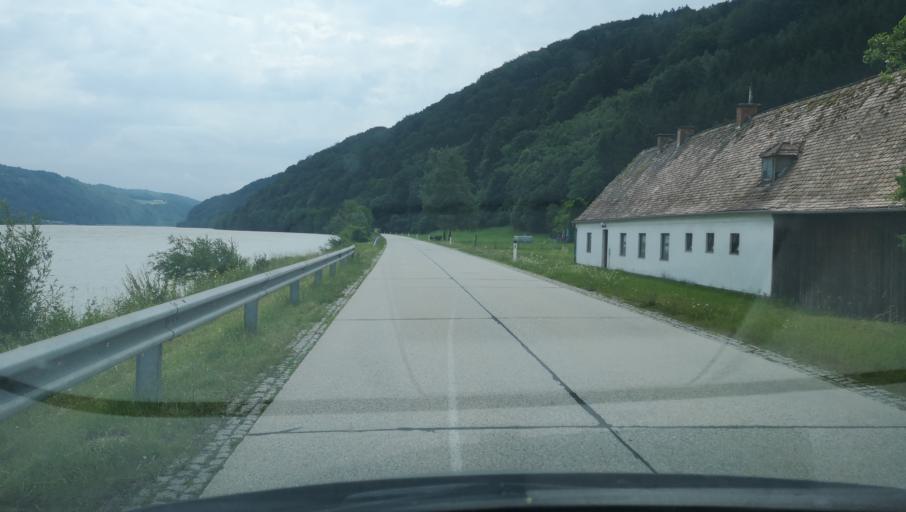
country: AT
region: Lower Austria
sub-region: Politischer Bezirk Melk
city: Nochling
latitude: 48.1913
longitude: 15.0154
